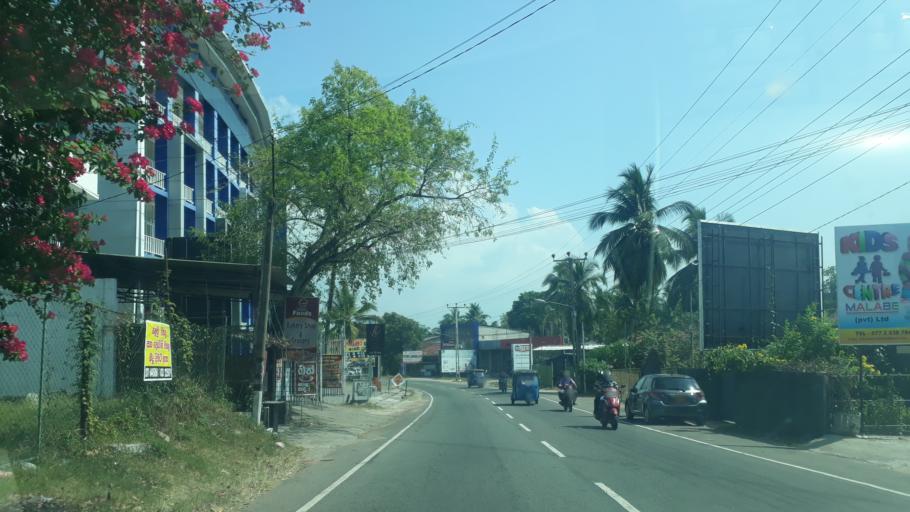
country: LK
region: Western
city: Gampaha
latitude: 7.0852
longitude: 80.0089
